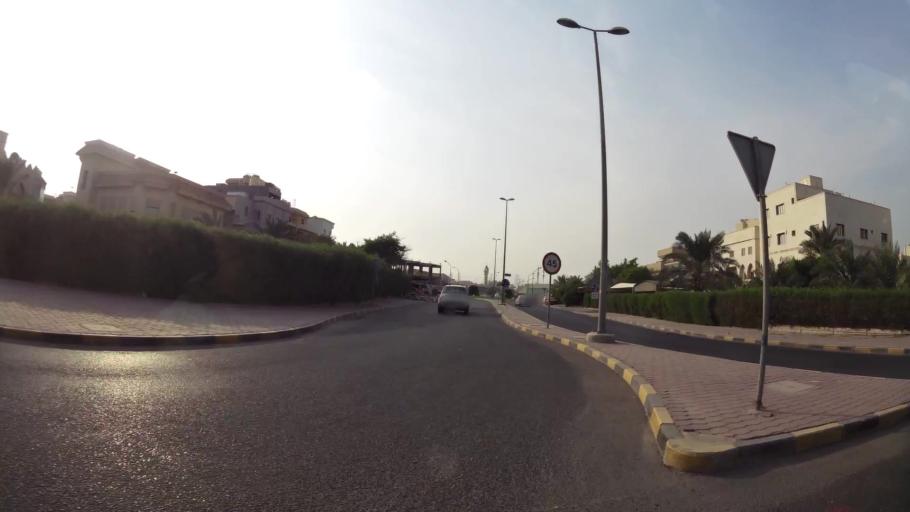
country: KW
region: Mubarak al Kabir
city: Sabah as Salim
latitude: 29.2310
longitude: 48.0612
